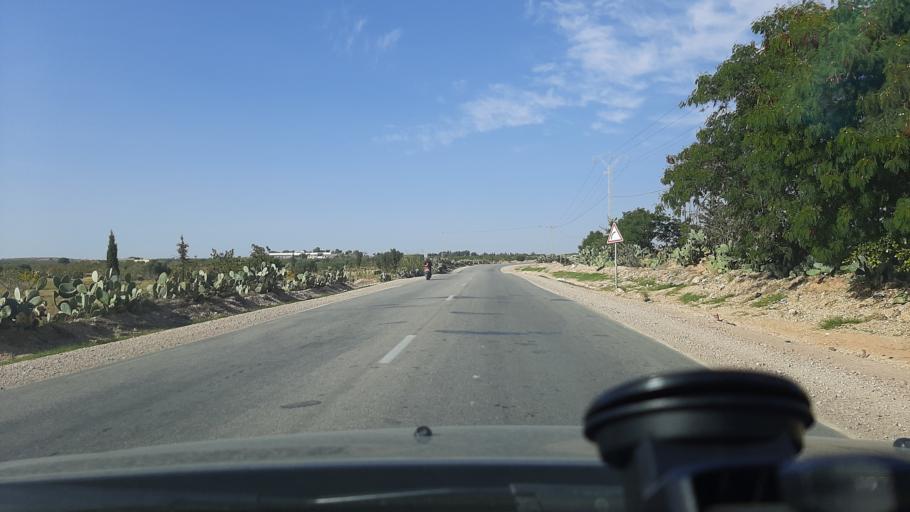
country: TN
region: Safaqis
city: Sfax
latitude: 34.8127
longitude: 10.6177
